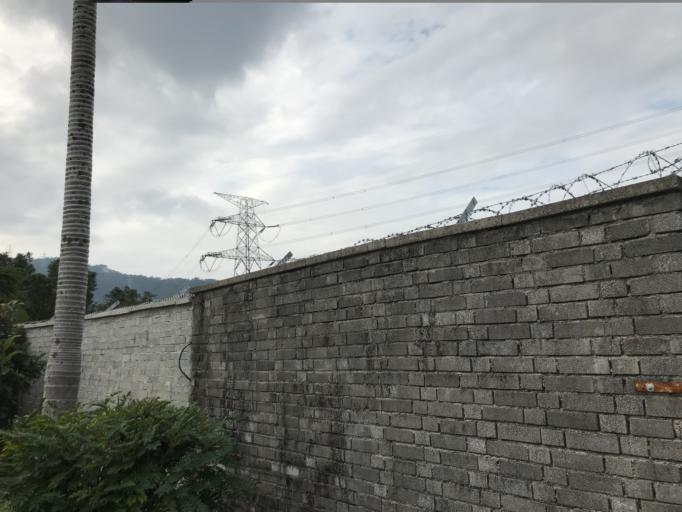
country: HK
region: Tai Po
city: Tai Po
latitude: 22.4659
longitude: 114.1568
